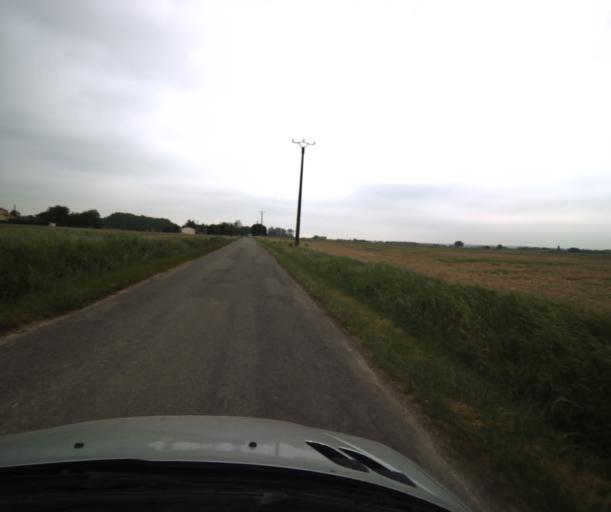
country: FR
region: Midi-Pyrenees
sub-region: Departement du Tarn-et-Garonne
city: Saint-Nicolas-de-la-Grave
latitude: 44.0487
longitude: 1.0215
